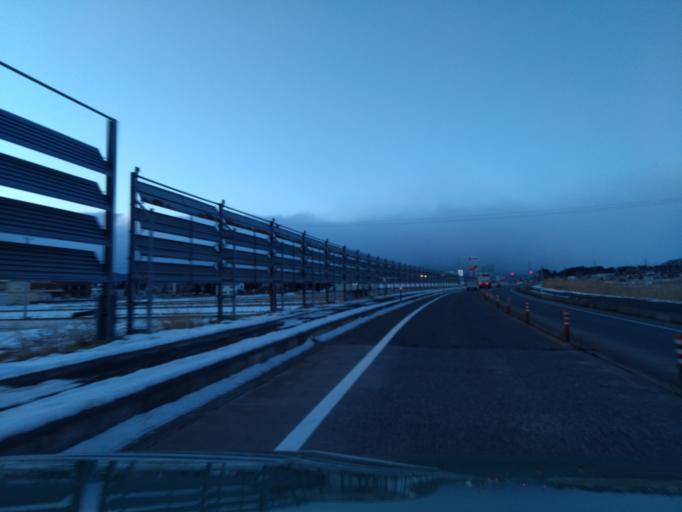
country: JP
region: Iwate
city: Shizukuishi
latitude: 39.6937
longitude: 140.9811
